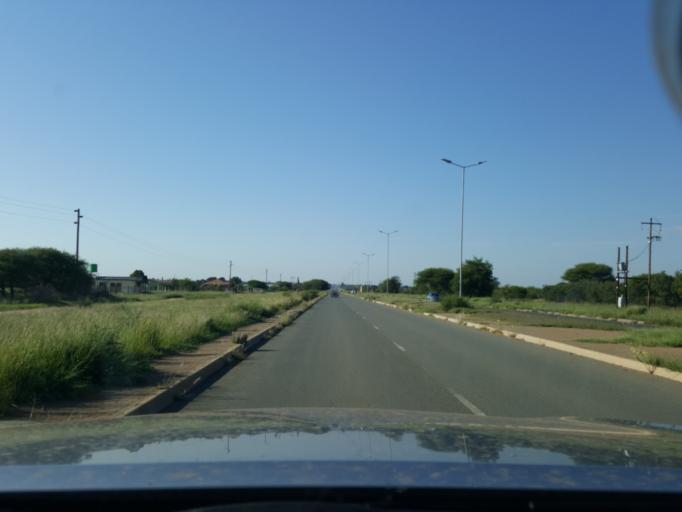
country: ZA
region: North-West
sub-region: Ngaka Modiri Molema District Municipality
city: Mmabatho
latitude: -25.7949
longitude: 25.6305
